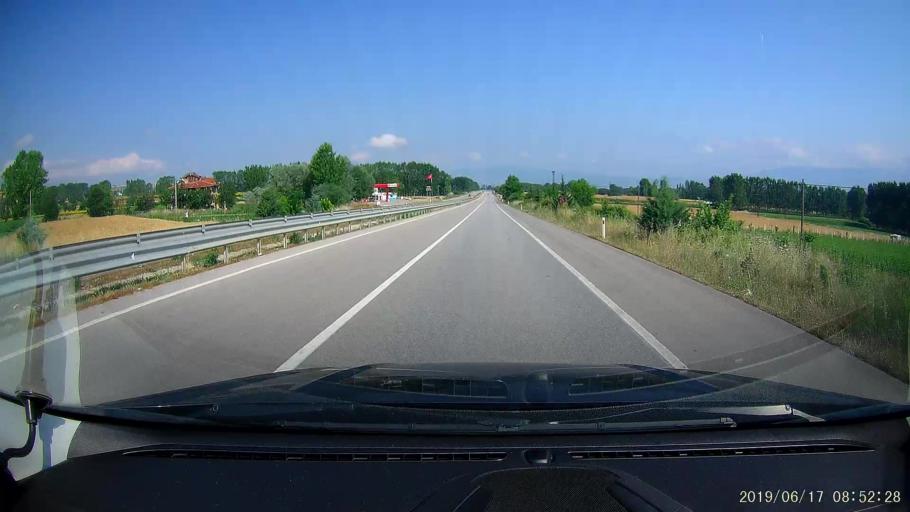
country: TR
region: Tokat
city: Erbaa
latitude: 40.6980
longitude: 36.4963
